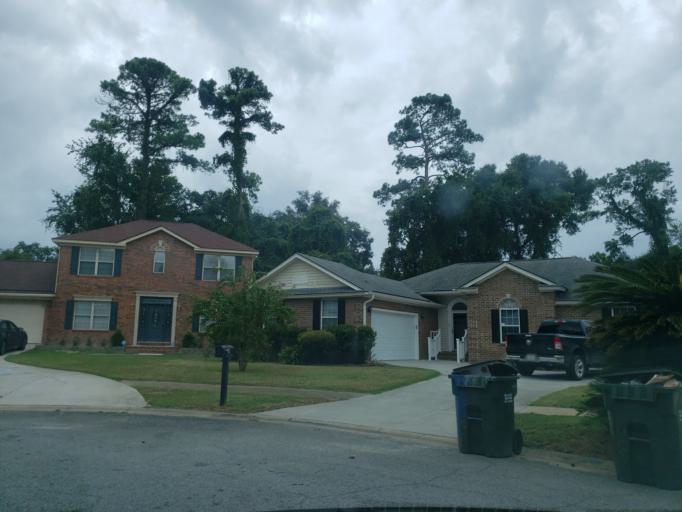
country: US
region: Georgia
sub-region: Chatham County
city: Wilmington Island
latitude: 32.0144
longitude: -80.9532
